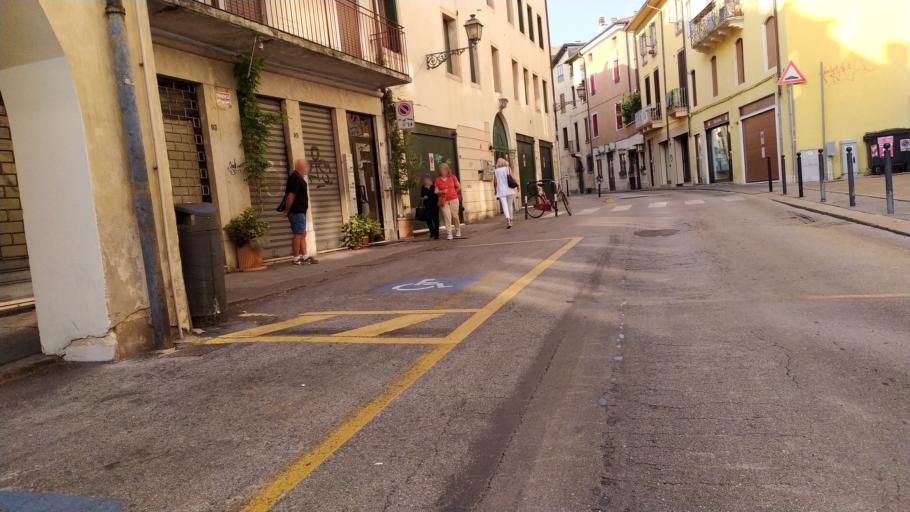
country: IT
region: Veneto
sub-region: Provincia di Vicenza
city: Vicenza
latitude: 45.5498
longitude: 11.5423
